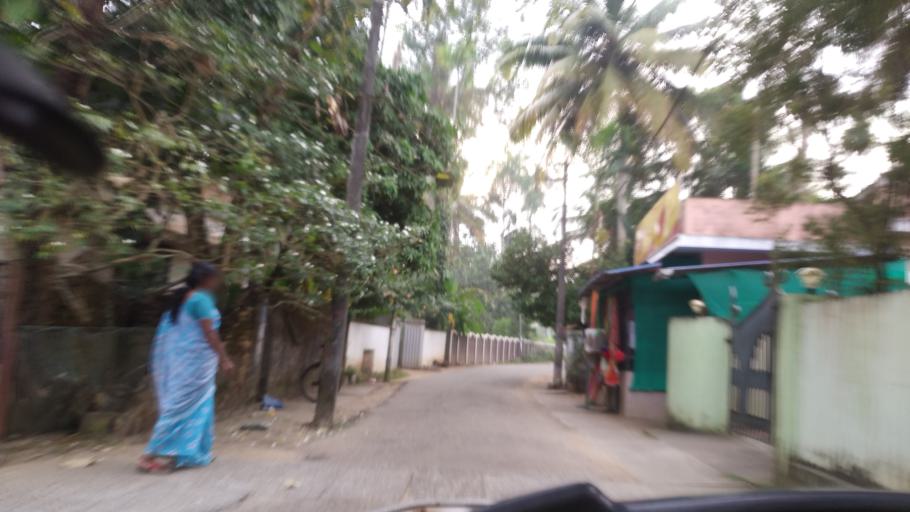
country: IN
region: Kerala
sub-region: Thrissur District
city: Kodungallur
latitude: 10.1343
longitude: 76.1984
